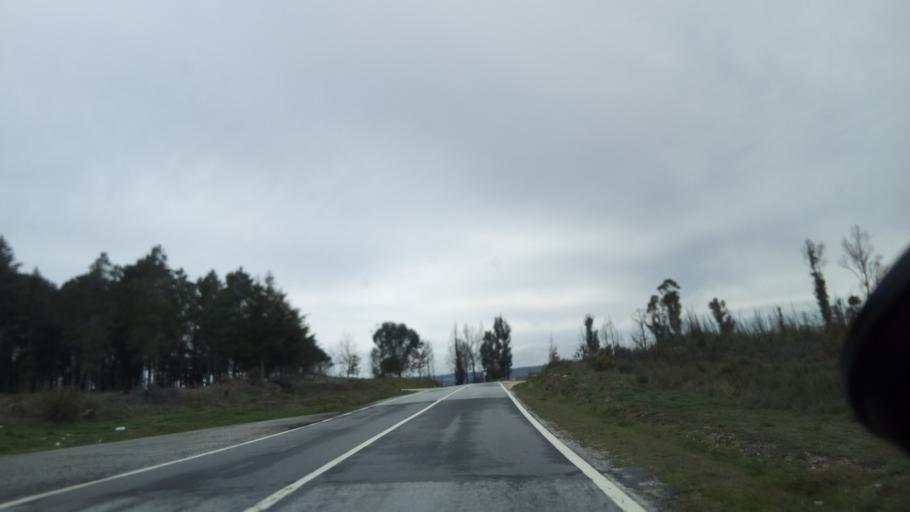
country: PT
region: Guarda
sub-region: Fornos de Algodres
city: Fornos de Algodres
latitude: 40.5230
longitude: -7.5980
